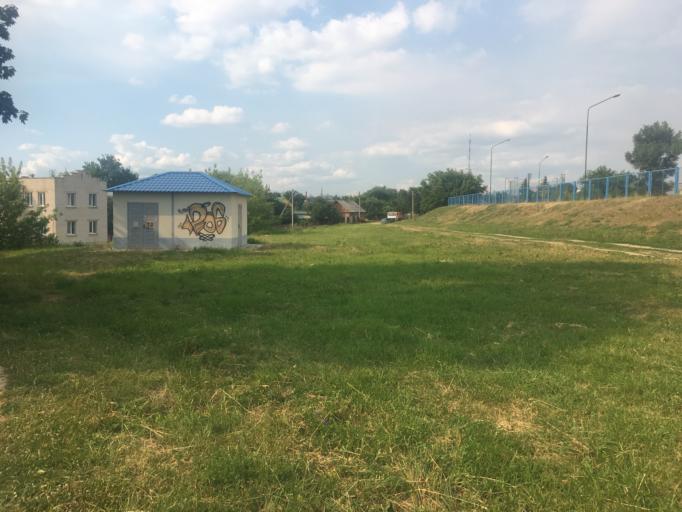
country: BY
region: Grodnenskaya
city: Hrodna
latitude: 53.6824
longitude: 23.8145
